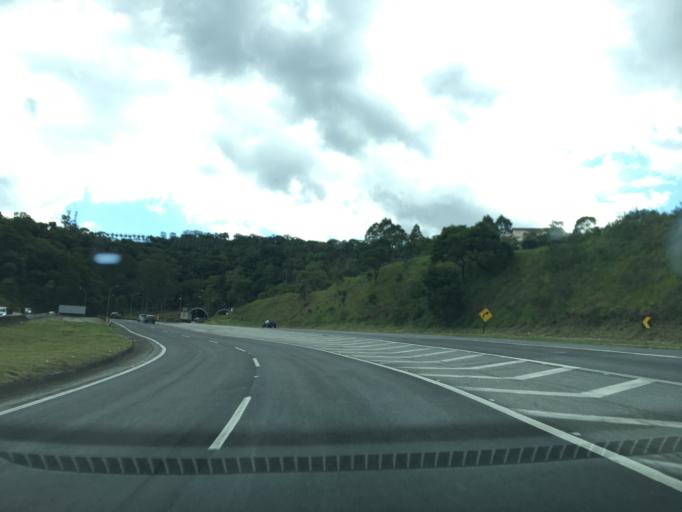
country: BR
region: Sao Paulo
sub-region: Mairipora
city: Mairipora
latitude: -23.3538
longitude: -46.5512
